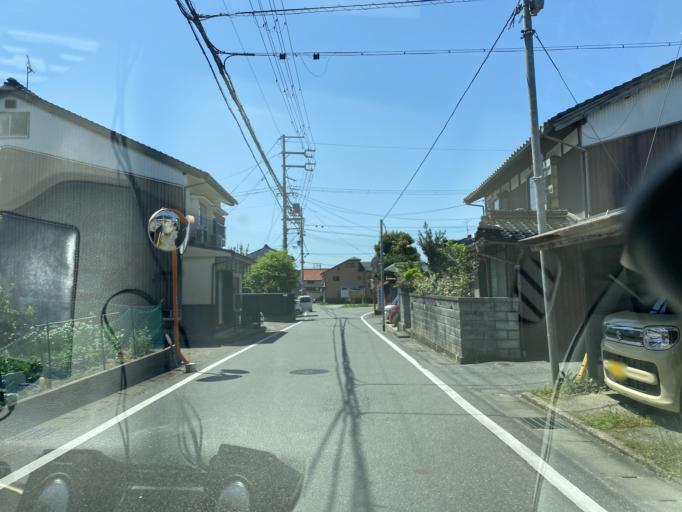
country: JP
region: Hyogo
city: Toyooka
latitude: 35.5385
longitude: 134.8196
